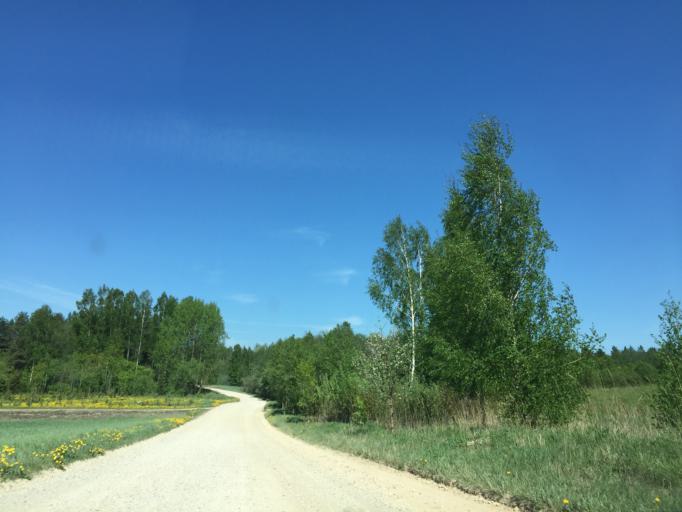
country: LV
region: Ikskile
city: Ikskile
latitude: 56.8695
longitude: 24.5023
